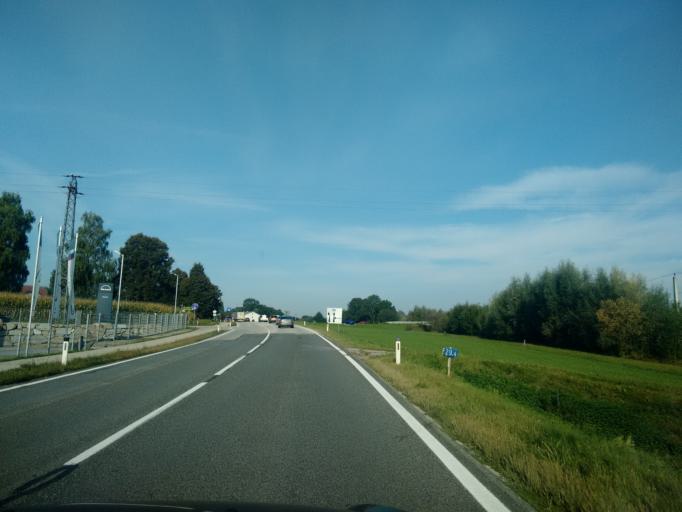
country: AT
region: Upper Austria
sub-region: Politischer Bezirk Grieskirchen
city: Grieskirchen
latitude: 48.2706
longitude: 13.7425
